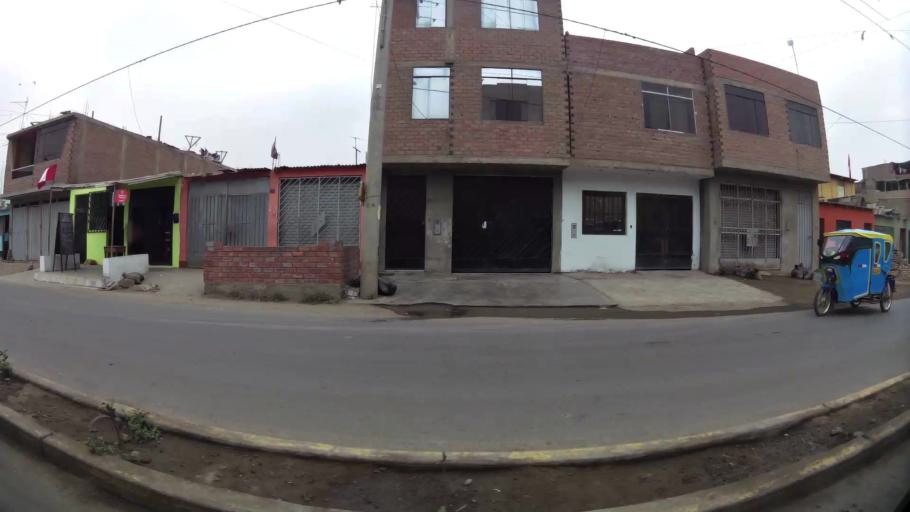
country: PE
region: Lima
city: Ventanilla
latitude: -11.9286
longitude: -77.0780
